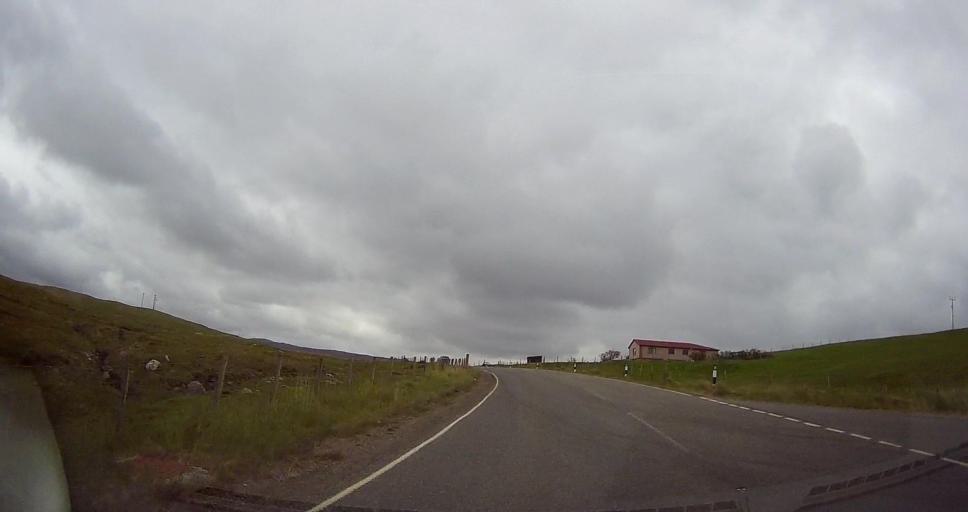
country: GB
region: Scotland
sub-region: Shetland Islands
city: Lerwick
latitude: 60.3811
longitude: -1.3426
